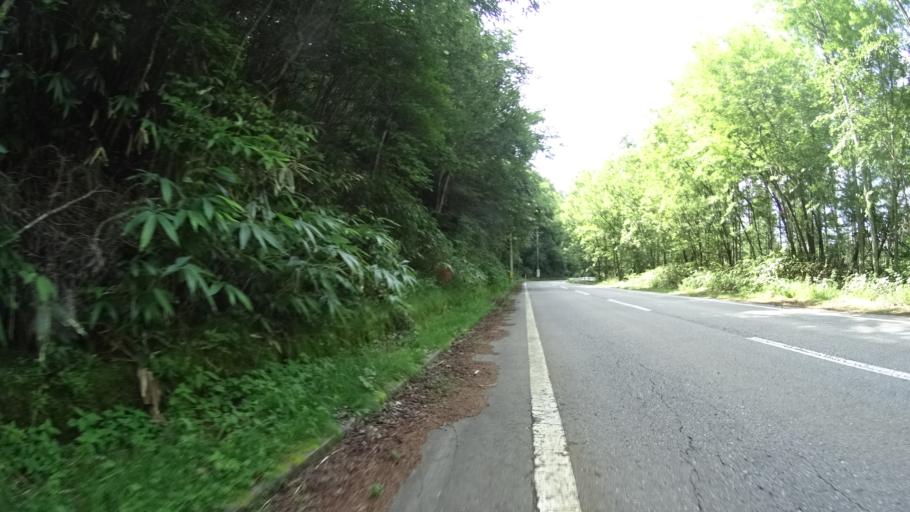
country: JP
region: Nagano
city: Saku
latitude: 36.0529
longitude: 138.3994
